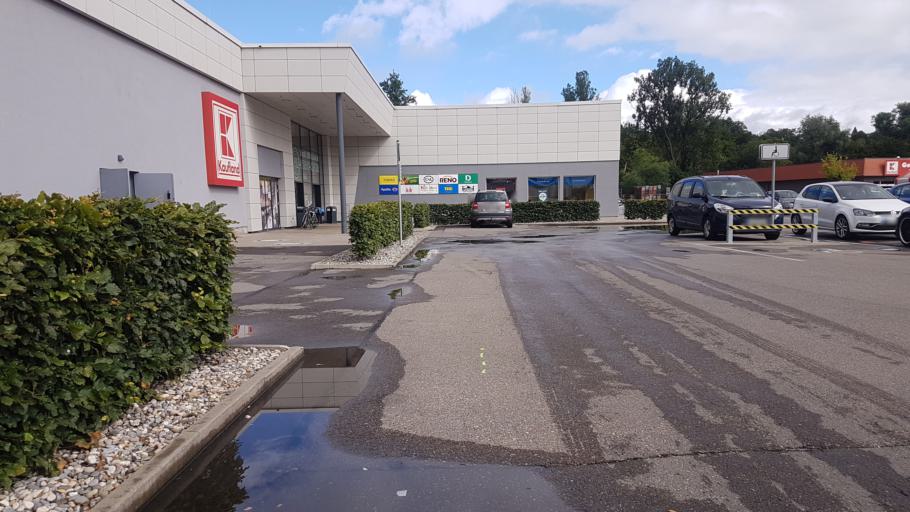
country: DE
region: Baden-Wuerttemberg
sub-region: Tuebingen Region
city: Ehingen
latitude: 48.2717
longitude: 9.7283
